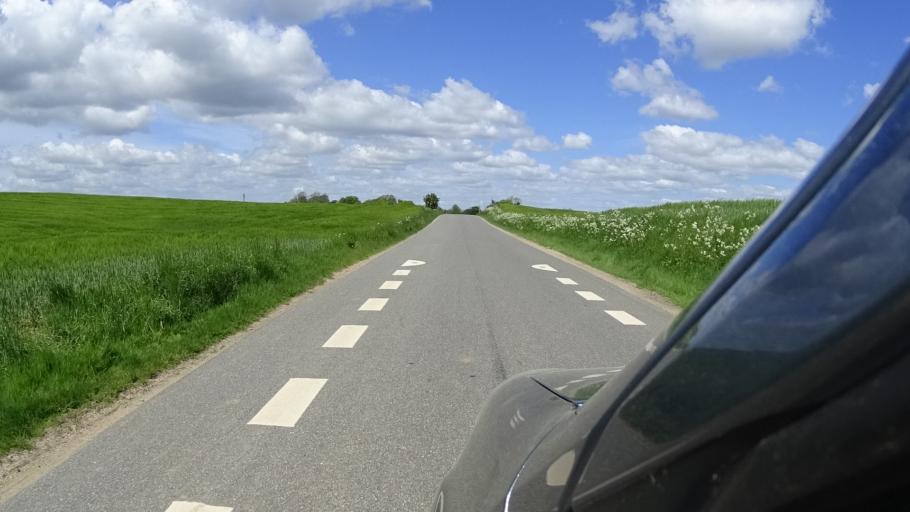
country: DK
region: South Denmark
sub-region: Vejle Kommune
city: Vejle
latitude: 55.6454
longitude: 9.5455
